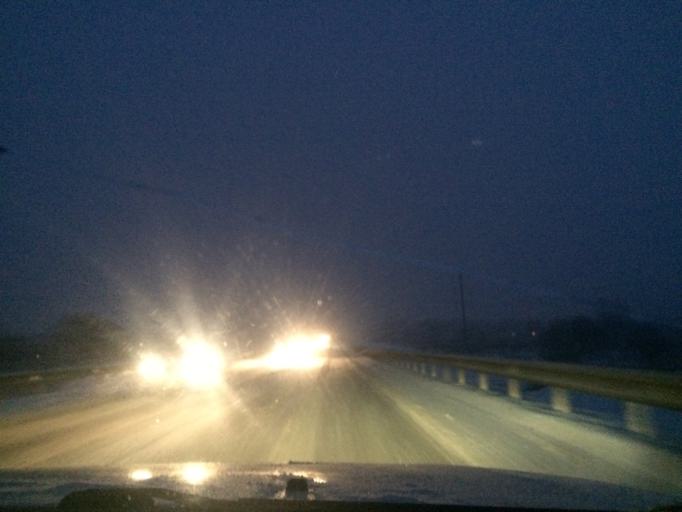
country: RU
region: Tula
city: Kosaya Gora
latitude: 54.1577
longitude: 37.5271
